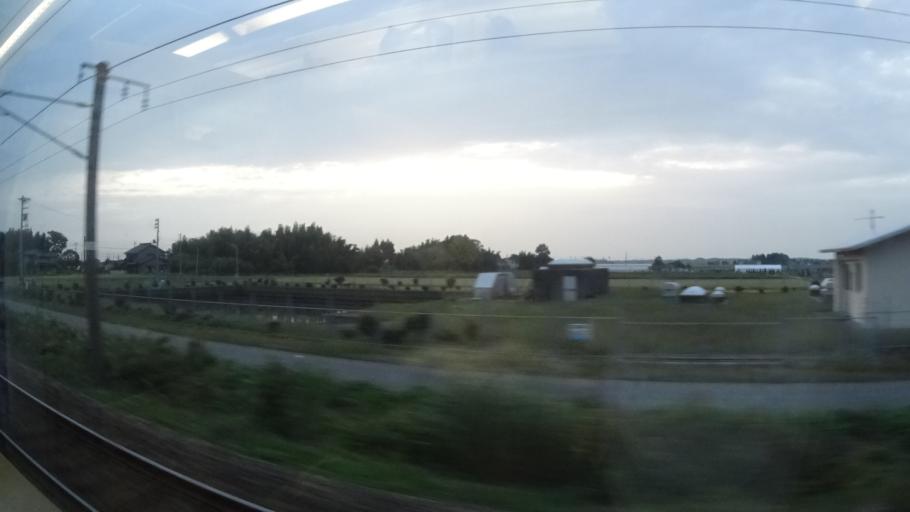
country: JP
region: Niigata
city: Murakami
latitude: 38.0852
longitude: 139.4217
